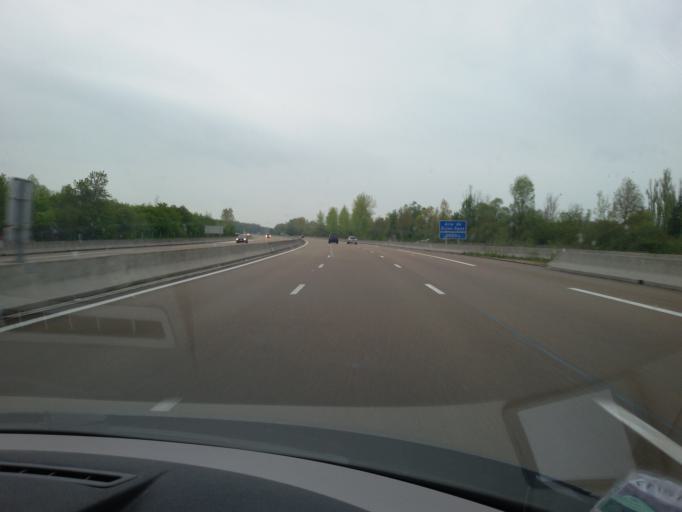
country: FR
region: Bourgogne
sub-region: Departement de la Cote-d'Or
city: Saint-Julien
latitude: 47.4039
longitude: 5.1828
